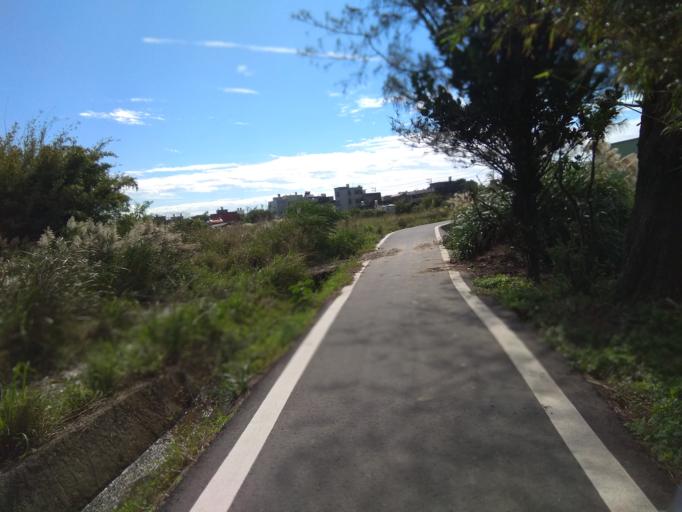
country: TW
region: Taiwan
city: Taoyuan City
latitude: 25.0472
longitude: 121.1208
